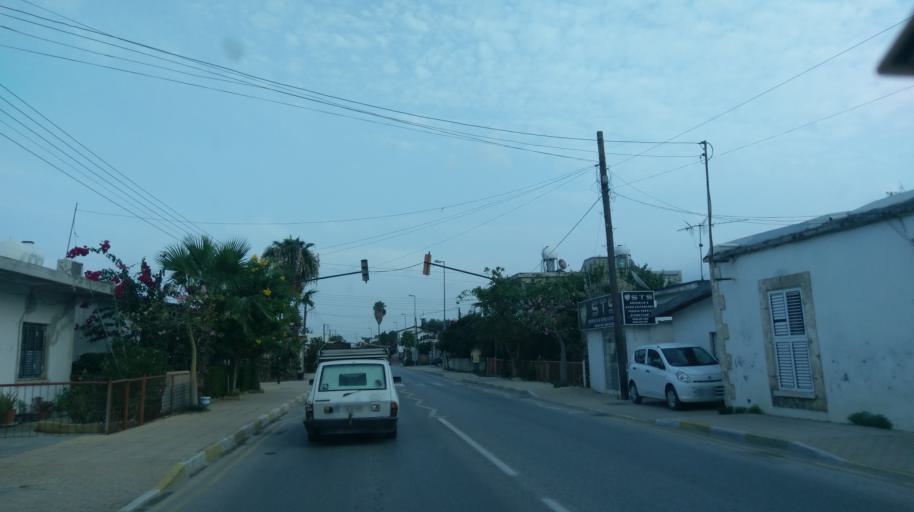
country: CY
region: Keryneia
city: Kyrenia
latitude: 35.3431
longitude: 33.2680
